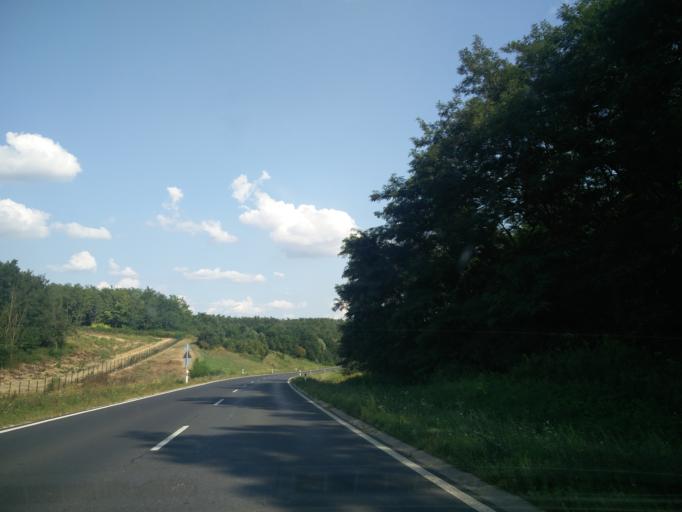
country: HU
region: Zala
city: Zalaegerszeg
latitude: 46.8796
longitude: 16.8447
